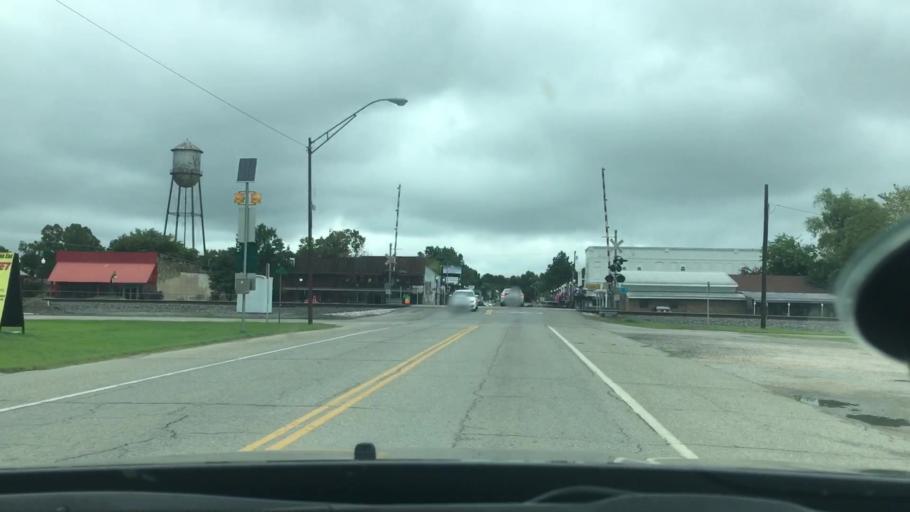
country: US
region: Oklahoma
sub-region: Sequoyah County
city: Vian
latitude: 35.4964
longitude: -94.9702
